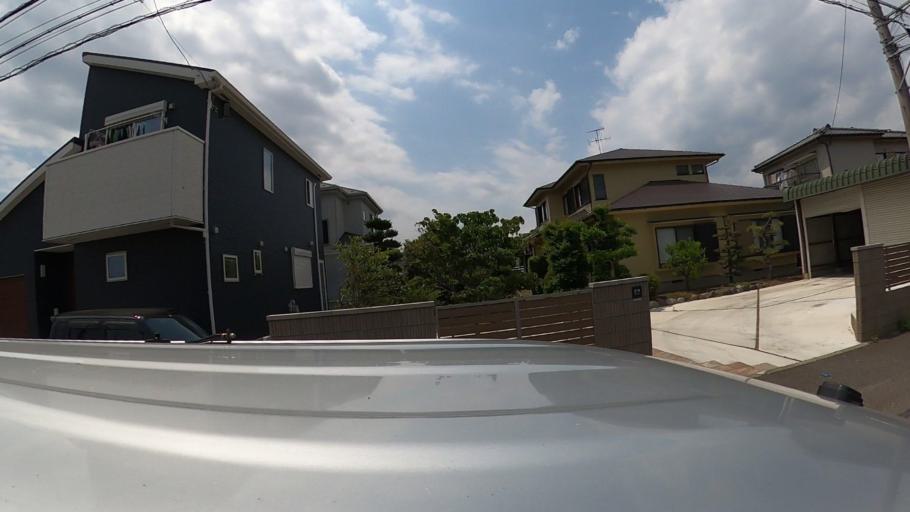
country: JP
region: Kanagawa
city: Chigasaki
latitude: 35.3818
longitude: 139.4013
